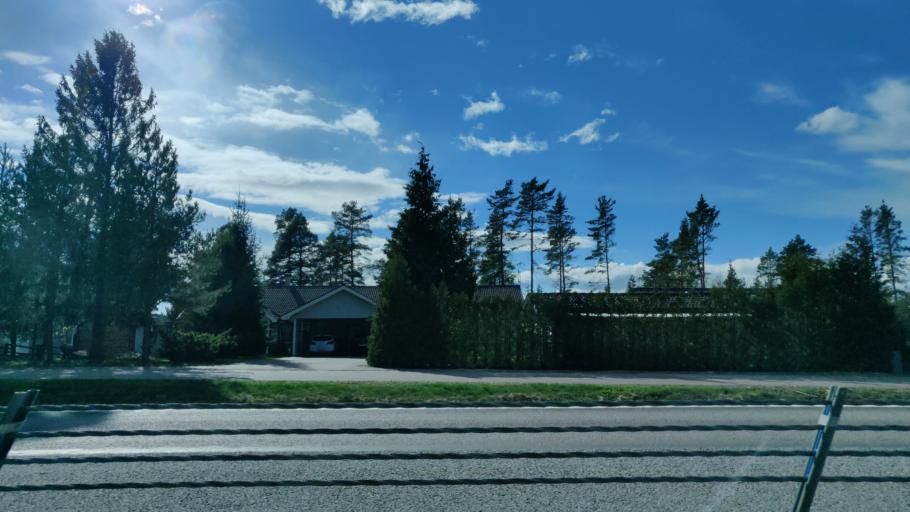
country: SE
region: Vaermland
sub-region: Forshaga Kommun
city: Forshaga
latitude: 59.4775
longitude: 13.4107
